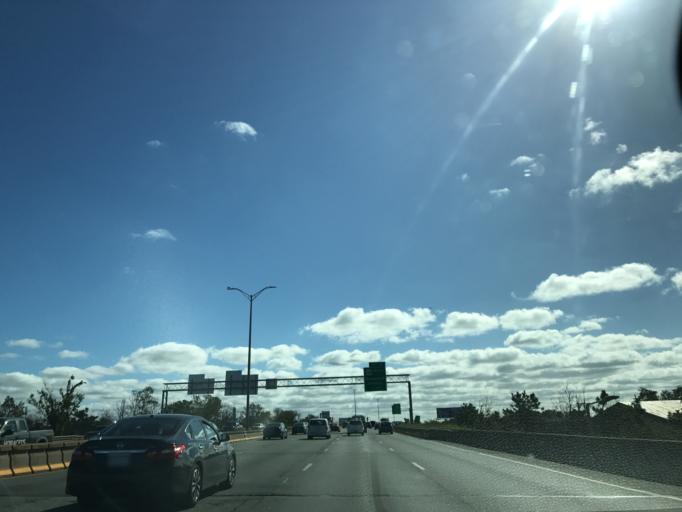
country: US
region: Massachusetts
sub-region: Suffolk County
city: South Boston
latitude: 42.2936
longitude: -71.0451
